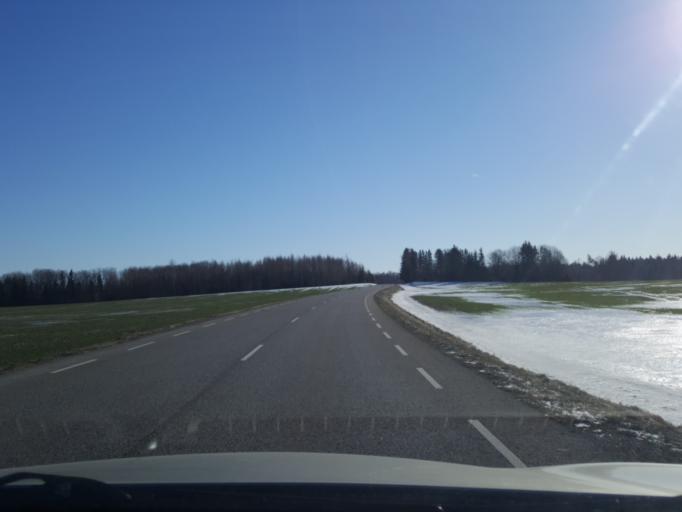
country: EE
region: Viljandimaa
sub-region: Vohma linn
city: Vohma
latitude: 58.5294
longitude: 25.6024
